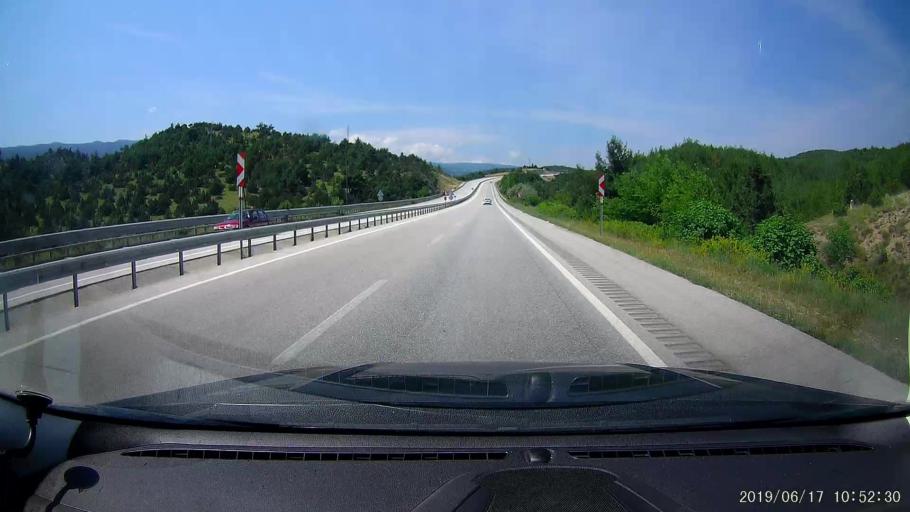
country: TR
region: Corum
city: Hacihamza
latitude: 41.0881
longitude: 34.3410
